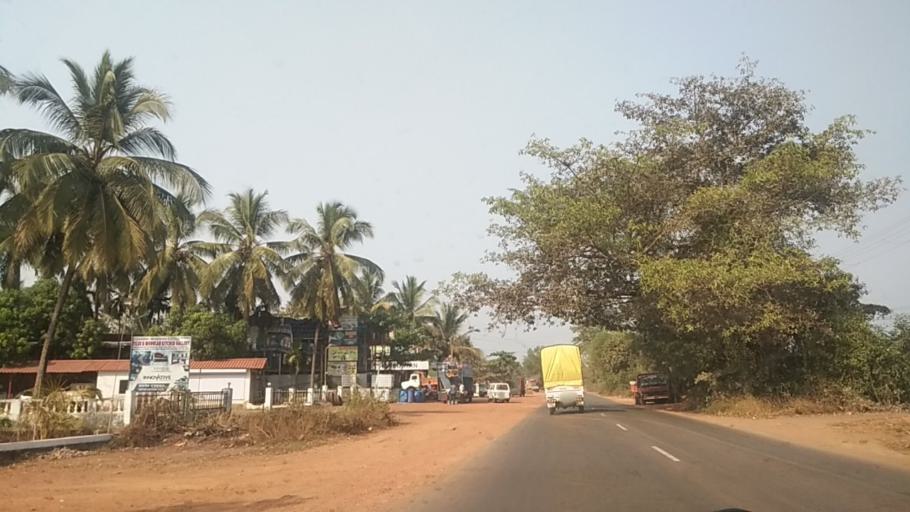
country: IN
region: Goa
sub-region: North Goa
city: Colovale
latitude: 15.6197
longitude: 73.8228
